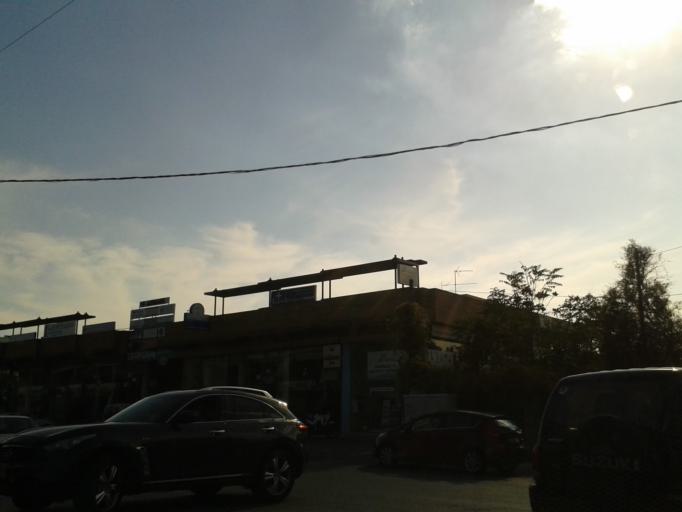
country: GR
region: Attica
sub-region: Nomarchia Anatolikis Attikis
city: Anoixi
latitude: 38.1357
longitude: 23.8572
